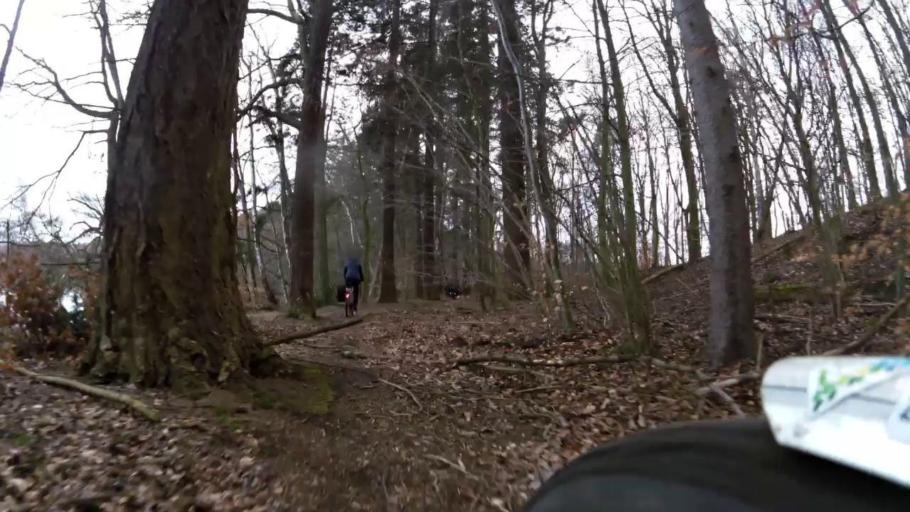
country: PL
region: West Pomeranian Voivodeship
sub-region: Powiat kamienski
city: Miedzyzdroje
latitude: 53.9424
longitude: 14.5604
